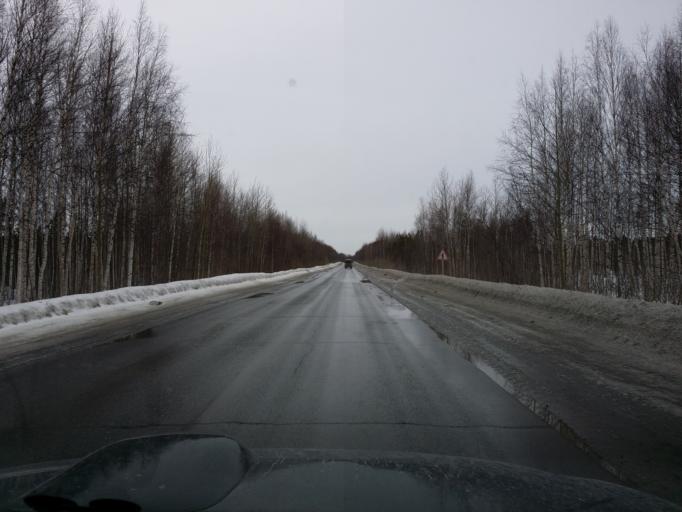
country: RU
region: Tomsk
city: Strezhevoy
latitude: 60.7428
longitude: 77.5288
